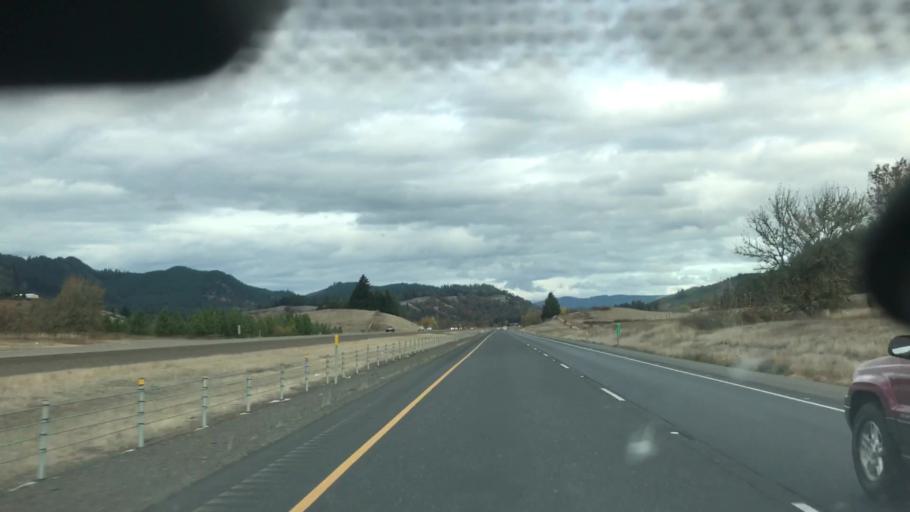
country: US
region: Oregon
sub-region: Douglas County
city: Yoncalla
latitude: 43.5815
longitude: -123.2601
